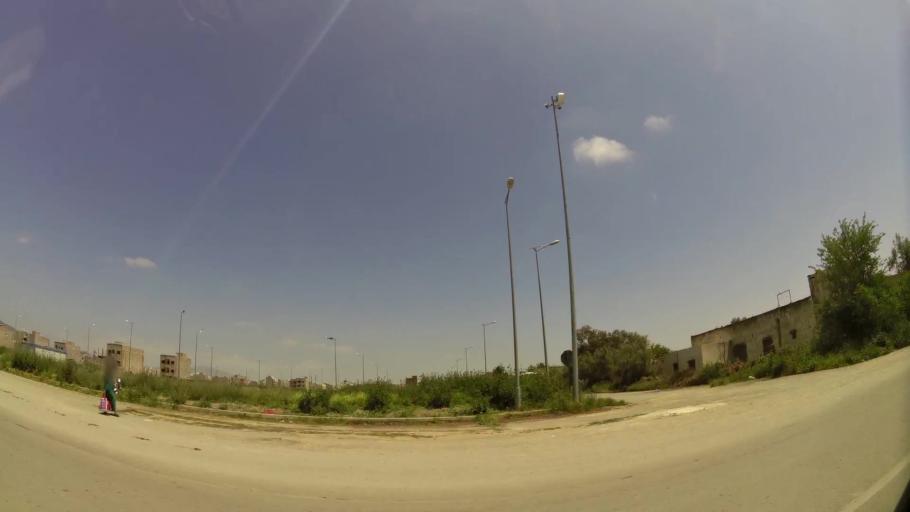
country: MA
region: Fes-Boulemane
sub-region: Fes
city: Fes
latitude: 34.0276
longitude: -5.0569
